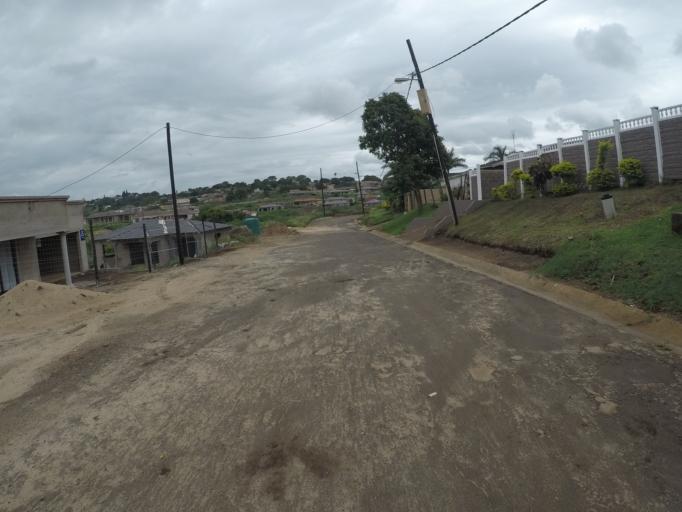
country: ZA
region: KwaZulu-Natal
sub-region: uThungulu District Municipality
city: Empangeni
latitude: -28.7798
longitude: 31.8568
